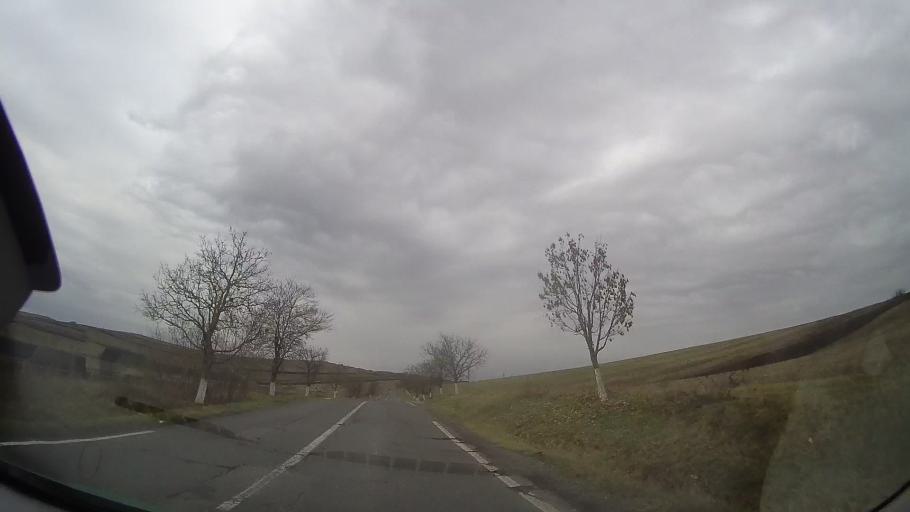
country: RO
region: Mures
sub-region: Comuna Faragau
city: Faragau
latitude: 46.7605
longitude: 24.5316
